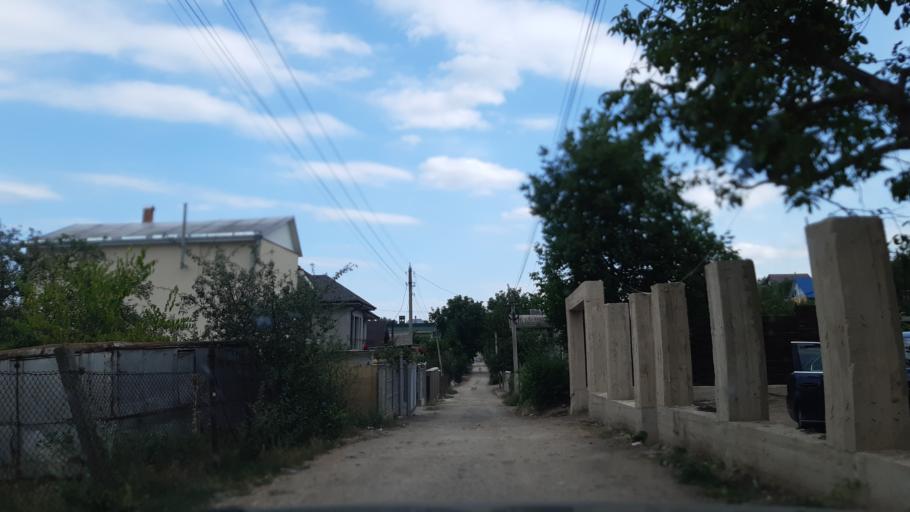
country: MD
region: Chisinau
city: Vatra
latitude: 47.0537
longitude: 28.7300
